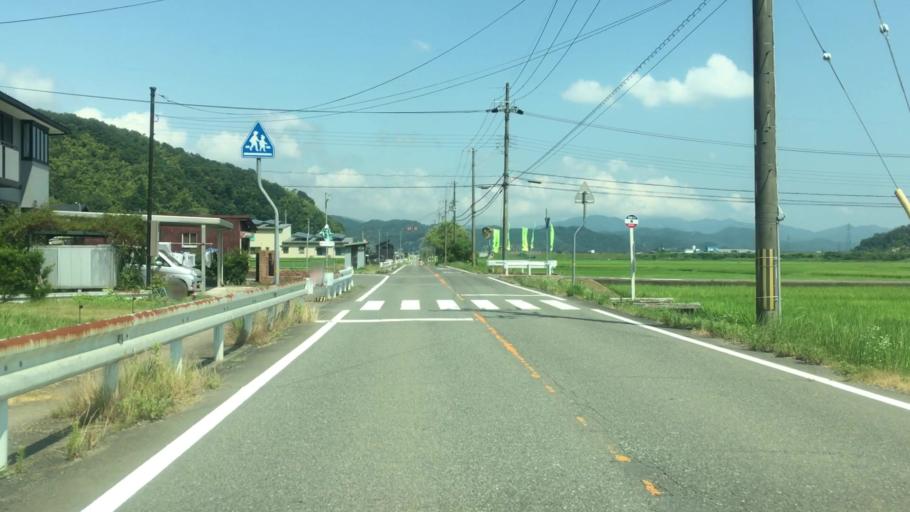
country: JP
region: Hyogo
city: Toyooka
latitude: 35.5674
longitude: 134.7915
